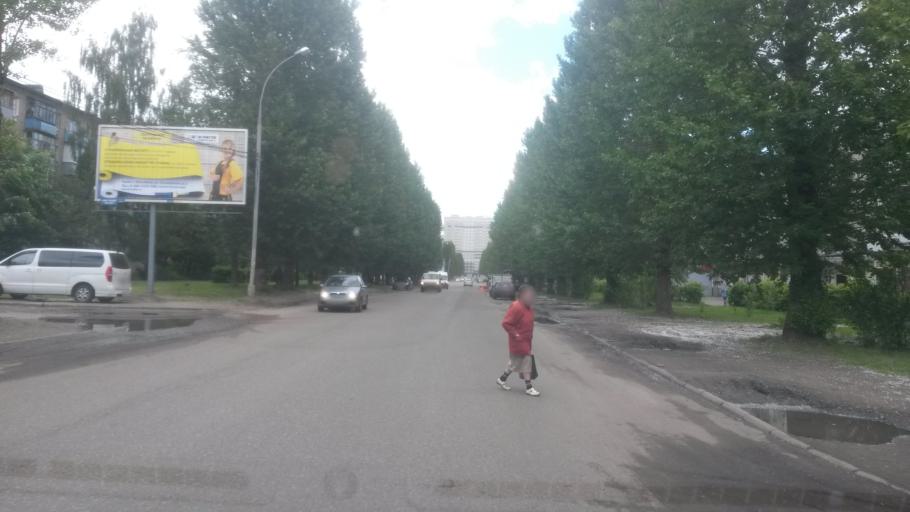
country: RU
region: Jaroslavl
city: Yaroslavl
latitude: 57.6824
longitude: 39.7966
